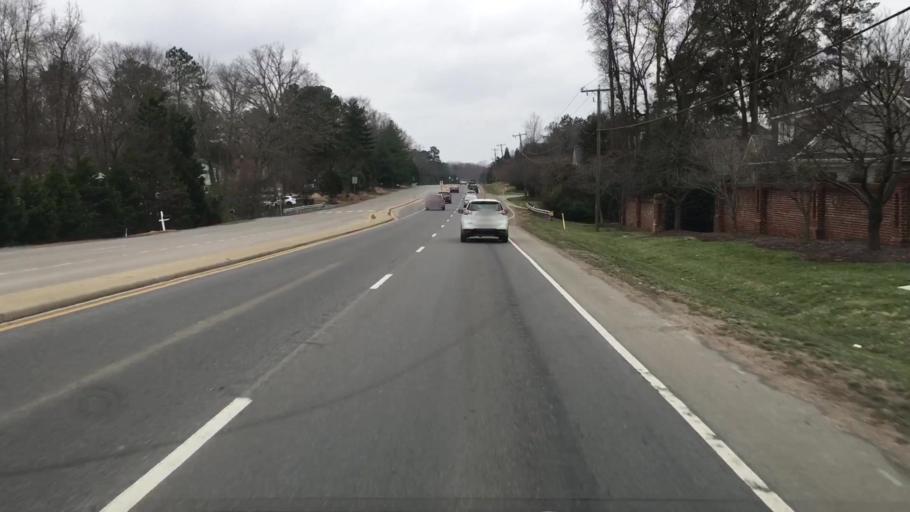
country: US
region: Virginia
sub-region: Chesterfield County
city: Bon Air
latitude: 37.5303
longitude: -77.5961
